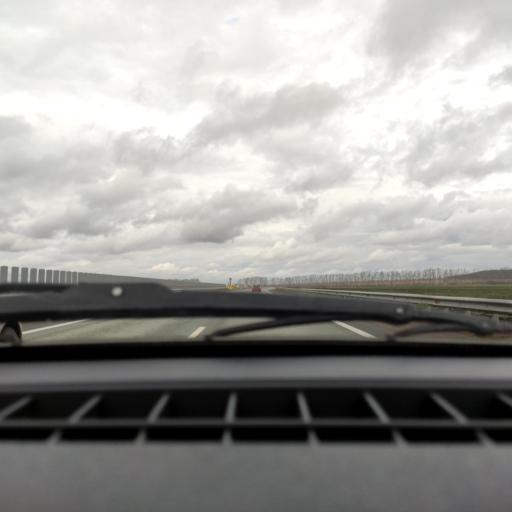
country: RU
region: Bashkortostan
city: Asanovo
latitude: 54.9503
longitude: 55.5837
